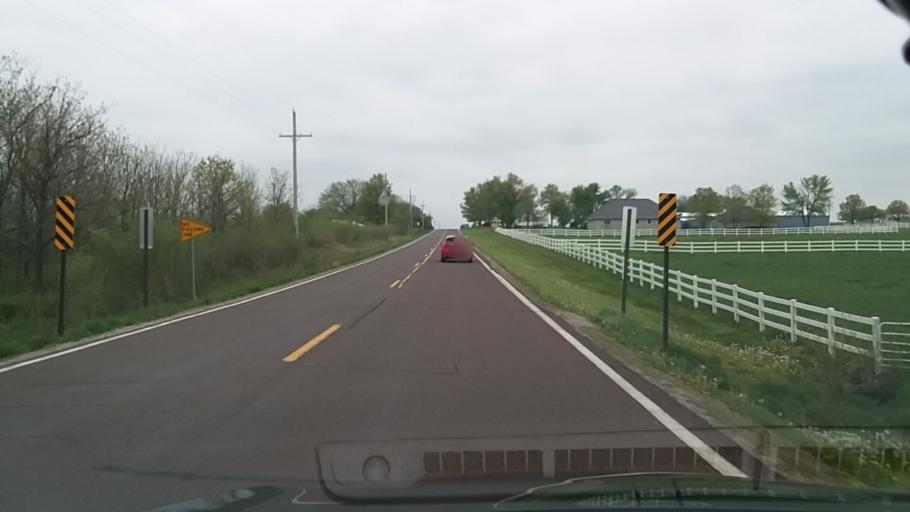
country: US
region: Kansas
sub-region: Johnson County
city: Edgerton
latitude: 38.8285
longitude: -95.0932
